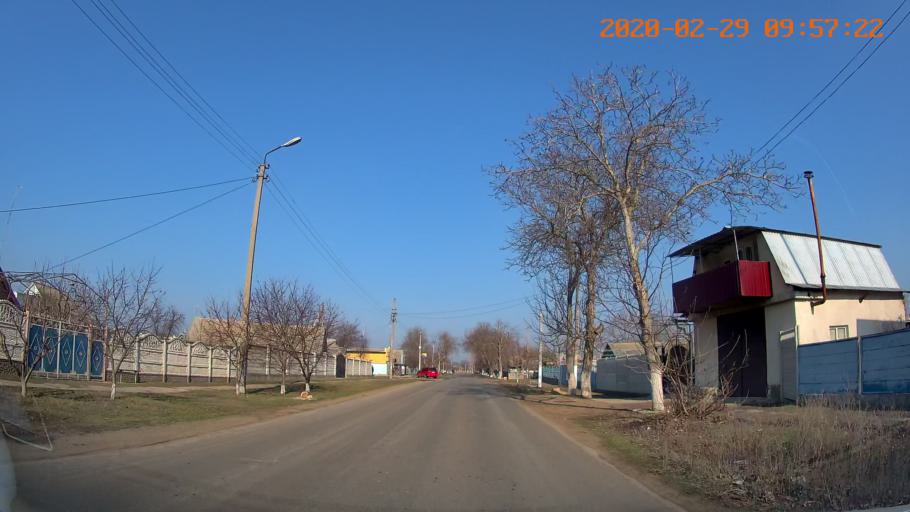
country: MD
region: Telenesti
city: Slobozia
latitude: 46.7498
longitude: 29.6995
